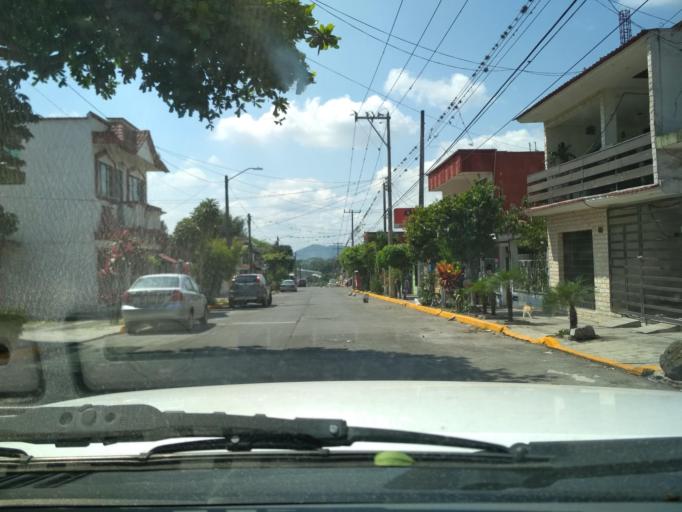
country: MX
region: Veracruz
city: Cordoba
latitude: 18.8784
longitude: -96.9151
